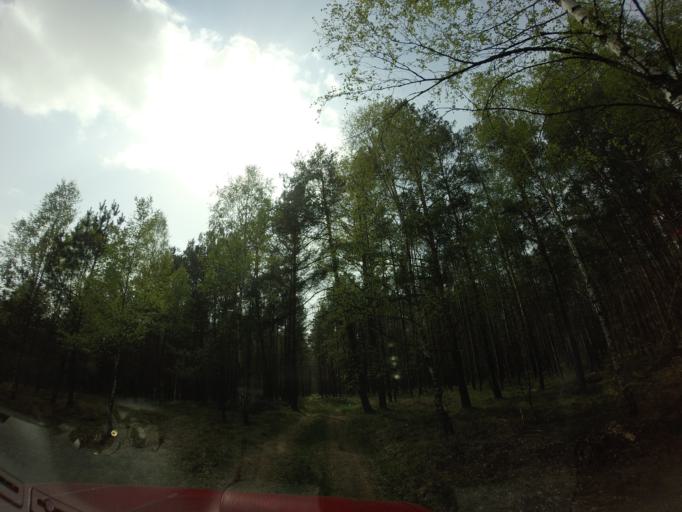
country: PL
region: West Pomeranian Voivodeship
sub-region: Powiat choszczenski
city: Drawno
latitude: 53.2708
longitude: 15.7159
